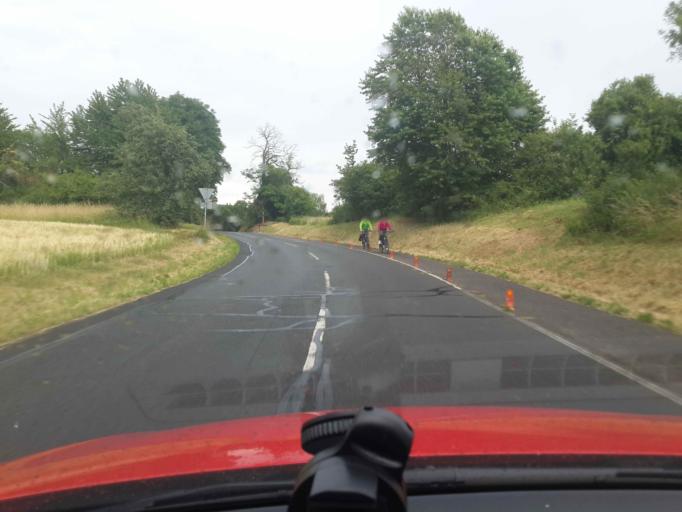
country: DE
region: Bavaria
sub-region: Regierungsbezirk Unterfranken
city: Worth am Main
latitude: 49.7967
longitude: 9.1456
